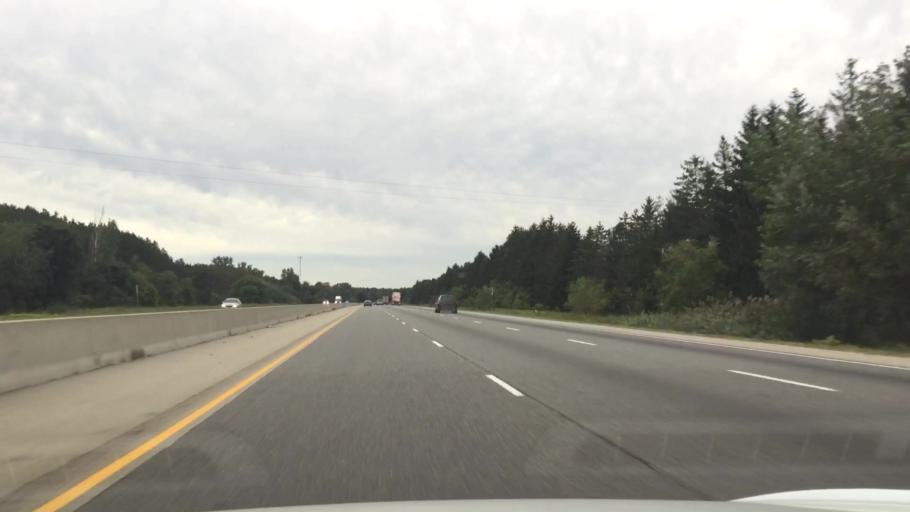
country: CA
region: Ontario
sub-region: Oxford County
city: Woodstock
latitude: 43.1848
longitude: -80.6437
